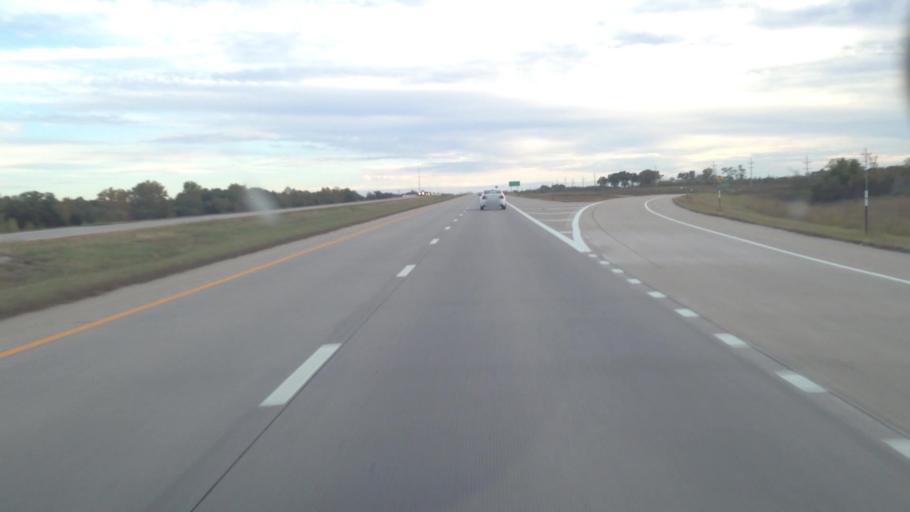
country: US
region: Kansas
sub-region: Franklin County
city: Ottawa
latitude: 38.7134
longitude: -95.2686
